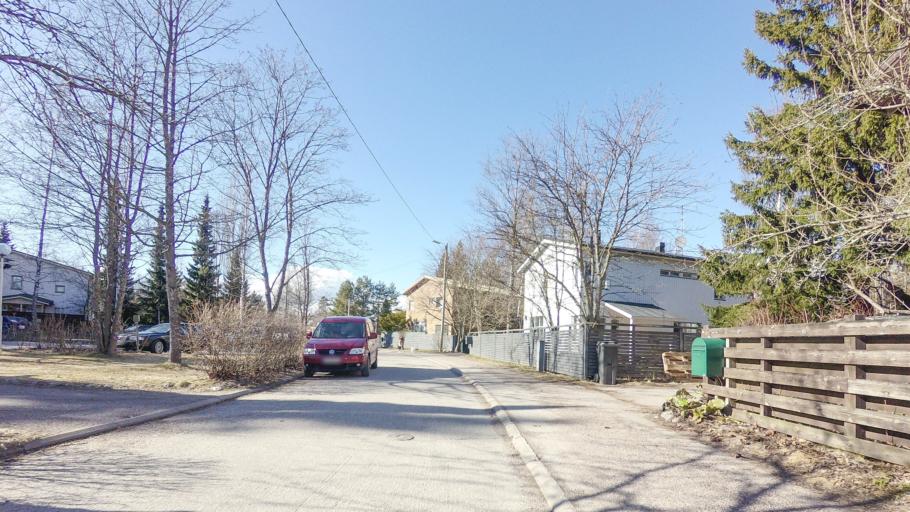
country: FI
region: Uusimaa
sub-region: Helsinki
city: Helsinki
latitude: 60.1614
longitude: 25.0675
